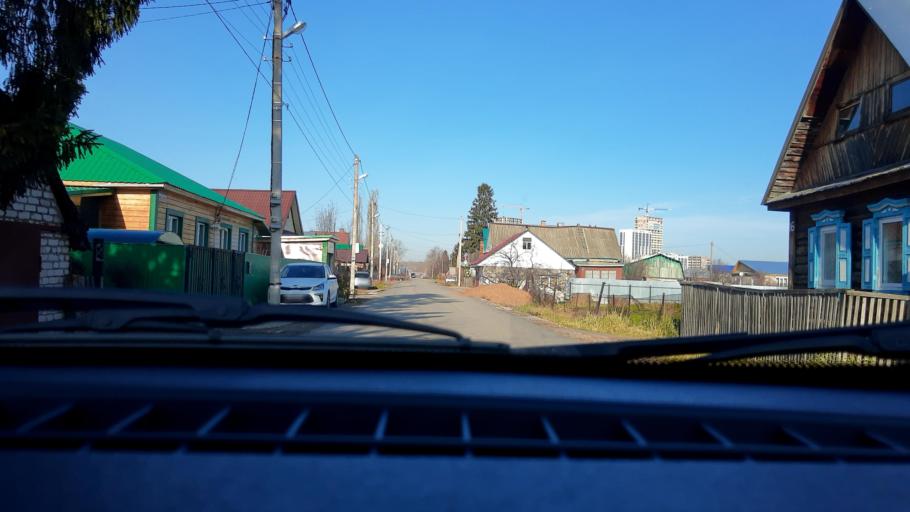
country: RU
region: Bashkortostan
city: Mikhaylovka
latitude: 54.7626
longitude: 55.9034
